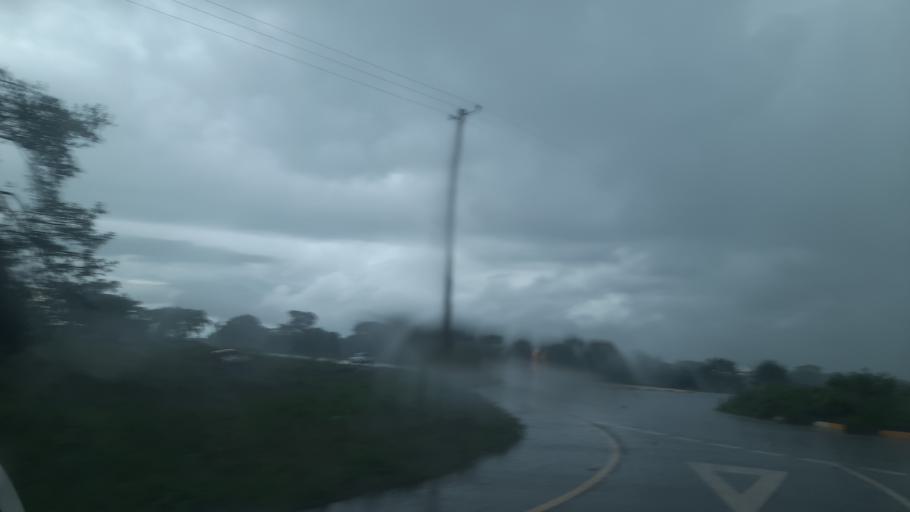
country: TZ
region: Arusha
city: Usa River
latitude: -3.4208
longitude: 36.7834
